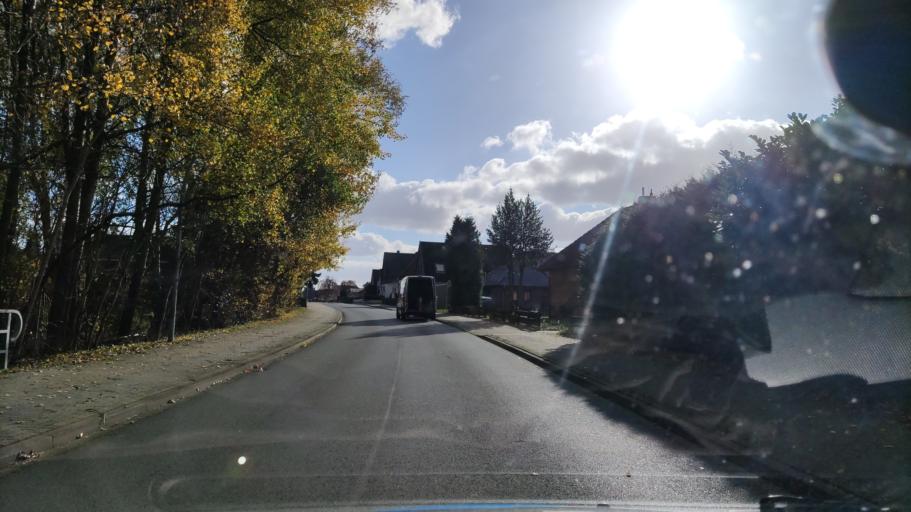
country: DE
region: Lower Saxony
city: Munster
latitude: 52.9976
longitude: 10.1030
